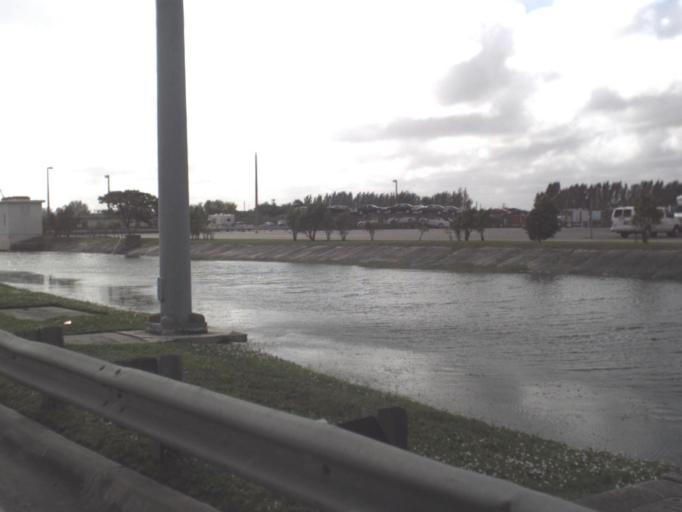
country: US
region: Florida
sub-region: Miami-Dade County
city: Virginia Gardens
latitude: 25.8040
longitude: -80.3051
